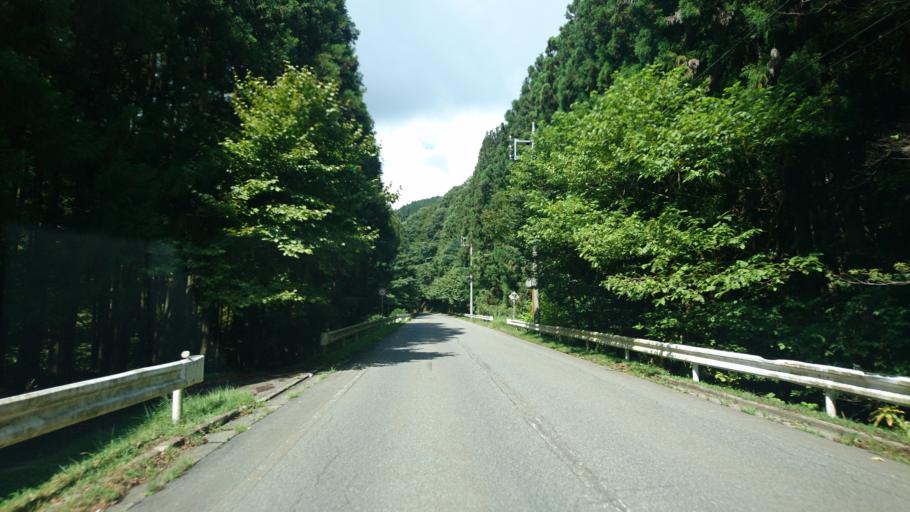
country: JP
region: Gunma
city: Omamacho-omama
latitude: 36.5642
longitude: 139.2468
